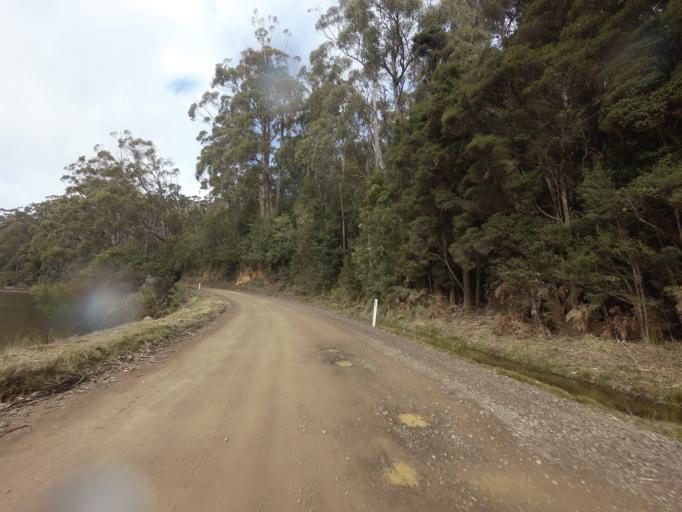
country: AU
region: Tasmania
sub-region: Huon Valley
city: Geeveston
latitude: -43.5663
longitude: 146.8869
